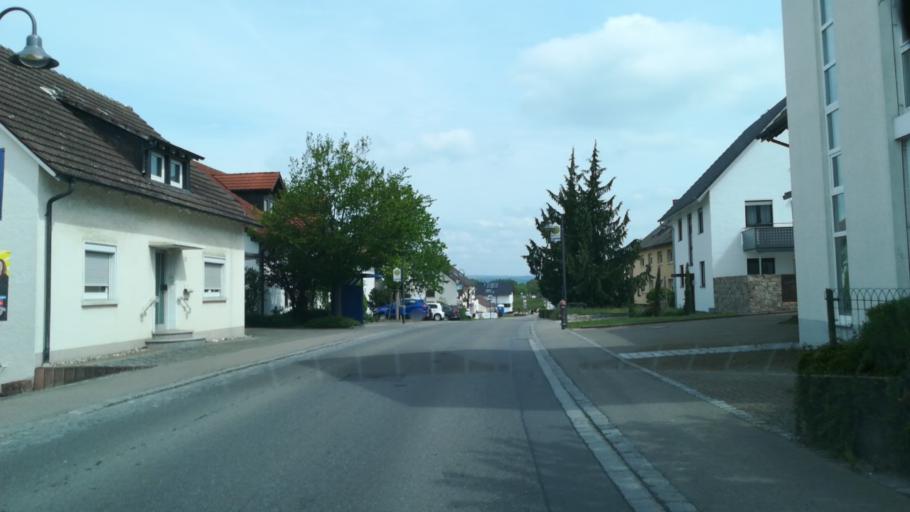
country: DE
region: Baden-Wuerttemberg
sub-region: Freiburg Region
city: Volkertshausen
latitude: 47.7889
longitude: 8.8763
